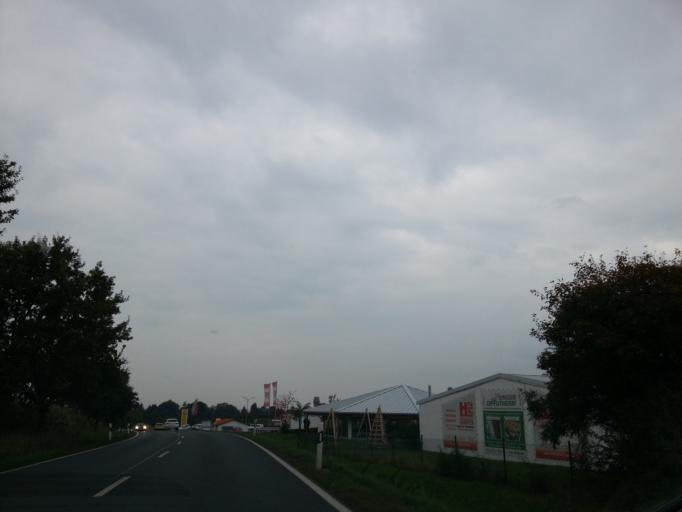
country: DE
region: Saxony
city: Nossen
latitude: 51.0476
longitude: 13.2923
